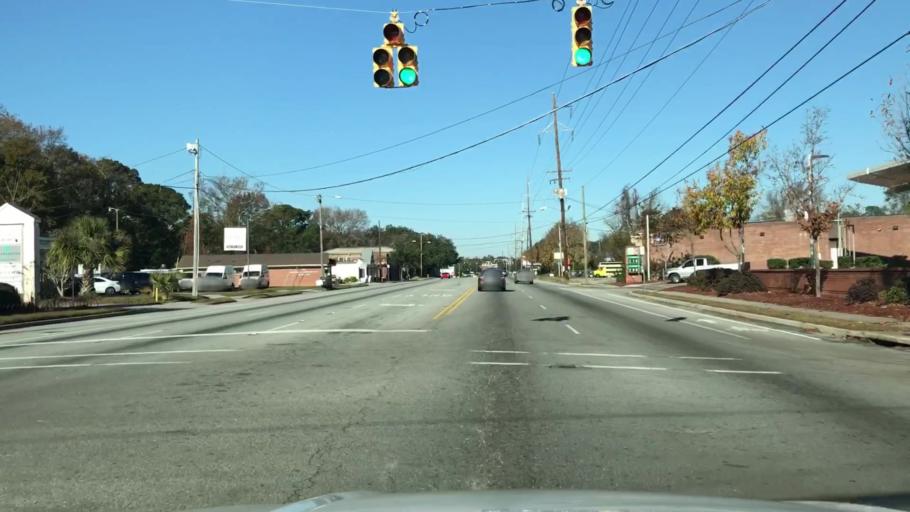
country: US
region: South Carolina
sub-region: Charleston County
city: Charleston
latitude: 32.7922
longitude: -79.9888
